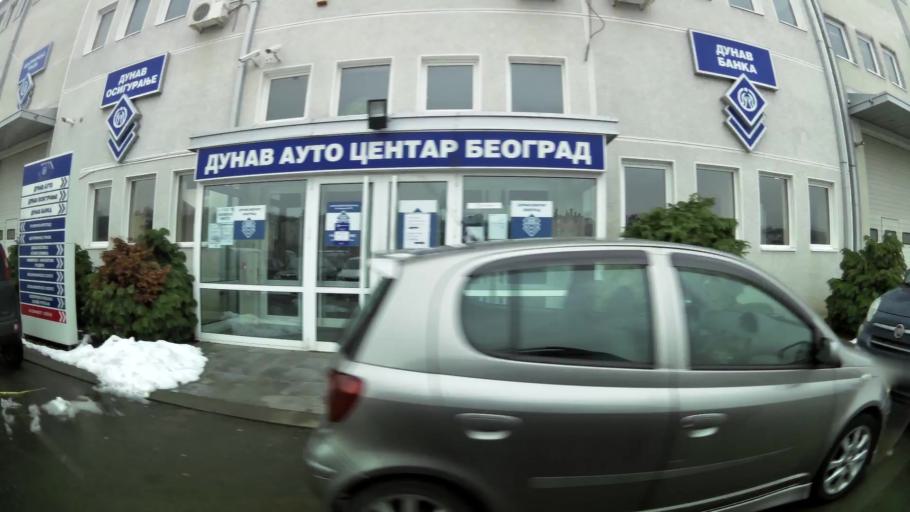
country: RS
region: Central Serbia
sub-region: Belgrade
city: Vozdovac
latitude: 44.7687
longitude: 20.4872
